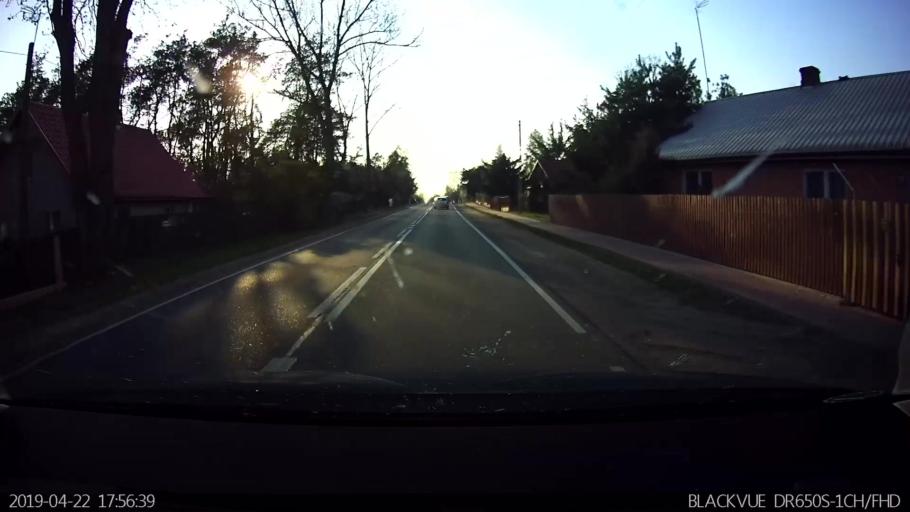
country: PL
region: Masovian Voivodeship
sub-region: Powiat wegrowski
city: Korytnica
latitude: 52.4658
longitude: 21.9041
